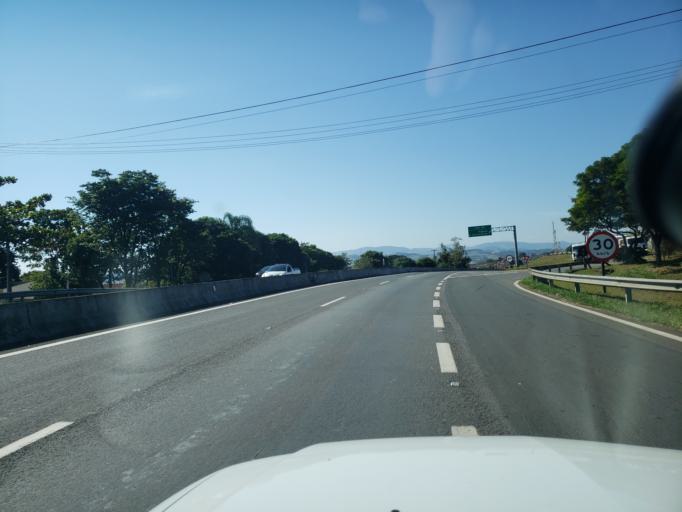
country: BR
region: Sao Paulo
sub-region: Itapira
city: Itapira
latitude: -22.4469
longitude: -46.8319
